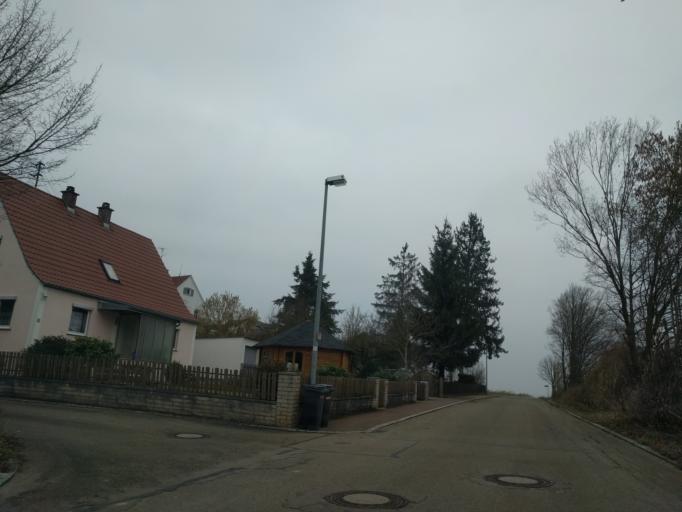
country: DE
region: Bavaria
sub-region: Swabia
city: Harburg
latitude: 48.7327
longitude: 10.7141
